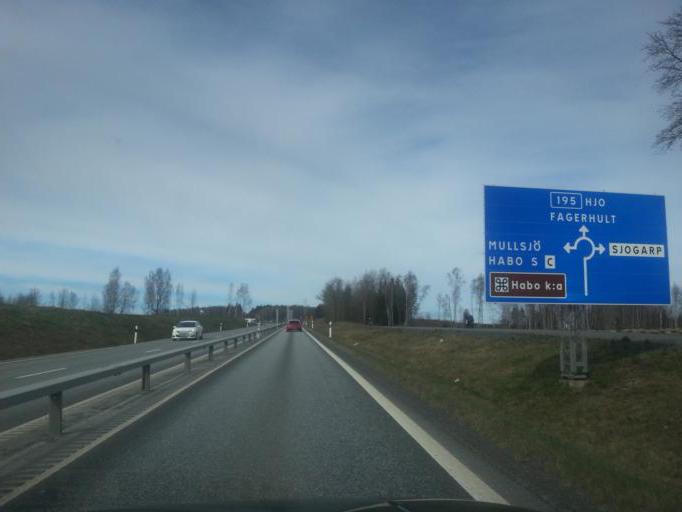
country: SE
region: Joenkoeping
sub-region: Habo Kommun
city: Habo
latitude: 57.8962
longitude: 14.1056
